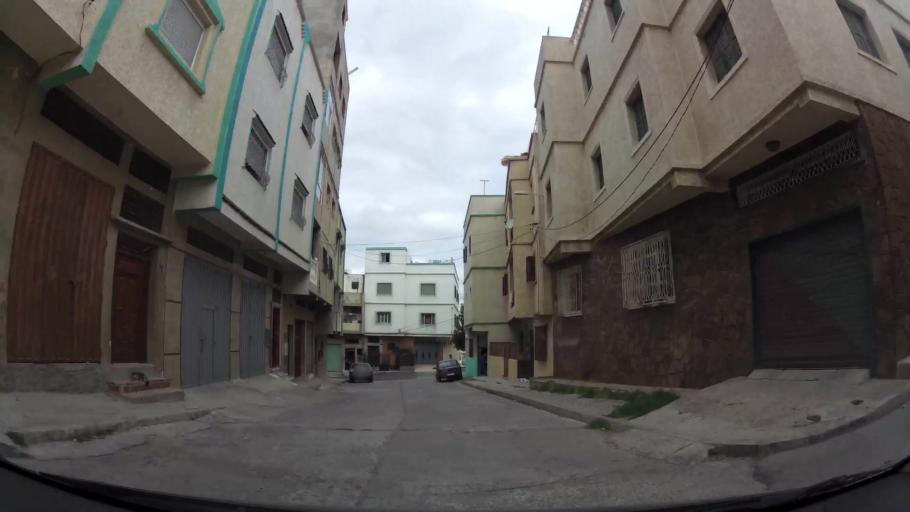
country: MA
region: Tanger-Tetouan
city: Tetouan
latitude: 35.5717
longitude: -5.3927
